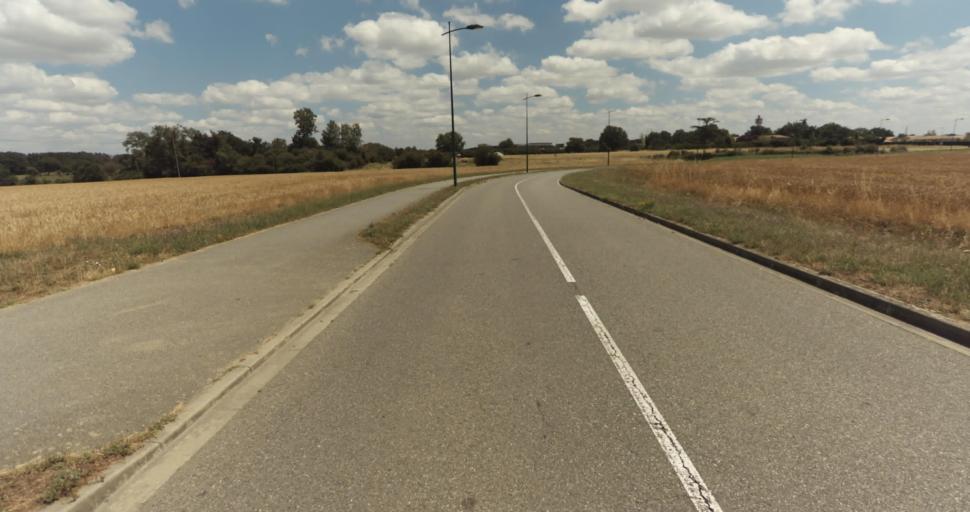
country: FR
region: Midi-Pyrenees
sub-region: Departement de la Haute-Garonne
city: Fontenilles
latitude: 43.5394
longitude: 1.1895
